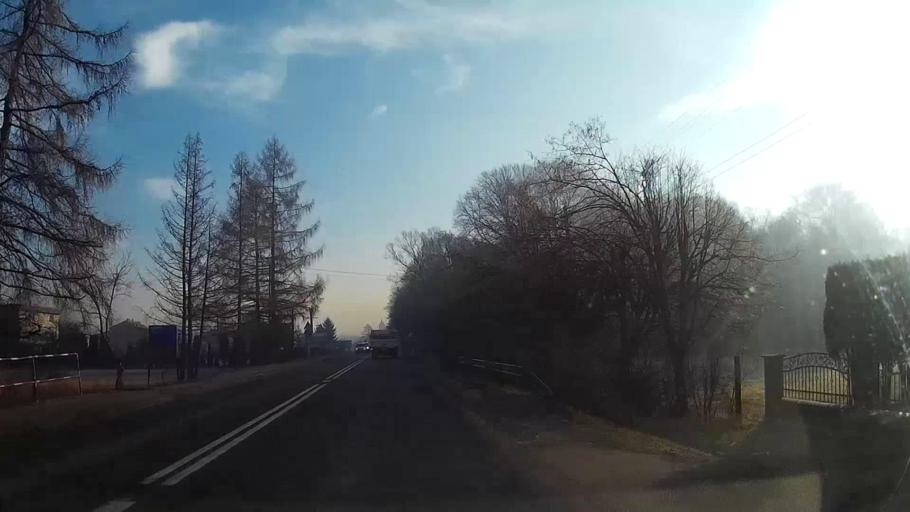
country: PL
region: Lesser Poland Voivodeship
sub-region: Powiat oswiecimski
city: Chelmek
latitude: 50.0716
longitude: 19.2506
